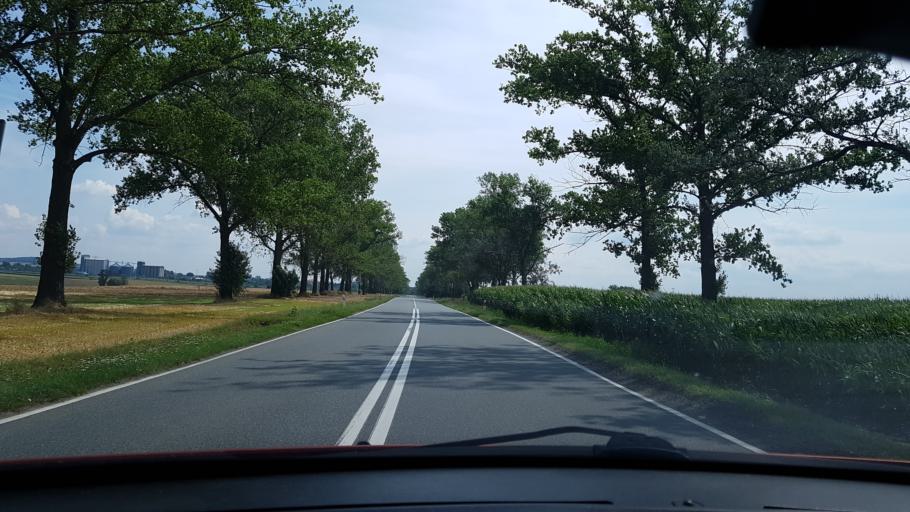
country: PL
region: Lower Silesian Voivodeship
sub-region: Powiat zabkowicki
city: Zabkowice Slaskie
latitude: 50.6080
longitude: 16.7865
